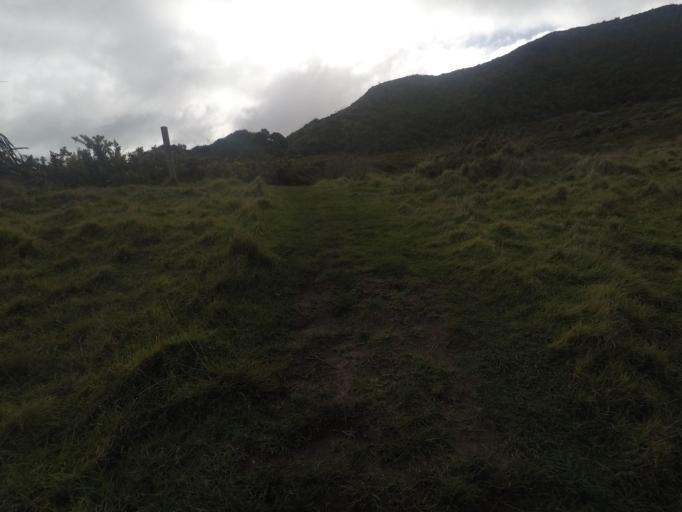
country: NZ
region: Auckland
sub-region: Auckland
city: Muriwai Beach
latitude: -36.8731
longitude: 174.4332
